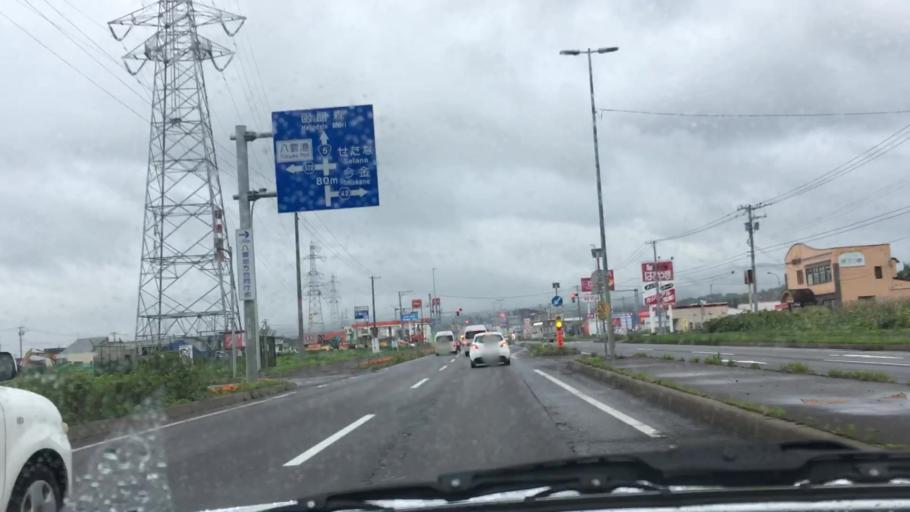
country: JP
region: Hokkaido
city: Nanae
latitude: 42.2531
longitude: 140.2838
